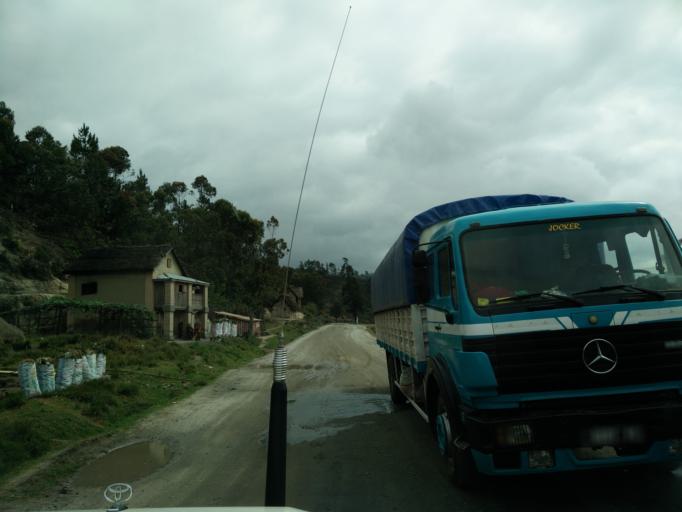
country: MG
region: Upper Matsiatra
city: Fianarantsoa
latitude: -21.2697
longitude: 47.2412
